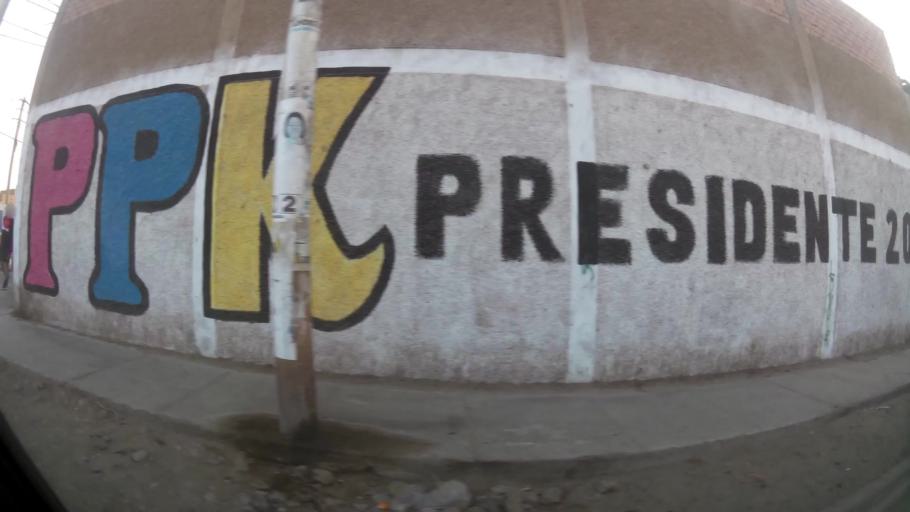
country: PE
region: Lima
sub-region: Huaura
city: Huacho
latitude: -11.1113
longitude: -77.6022
